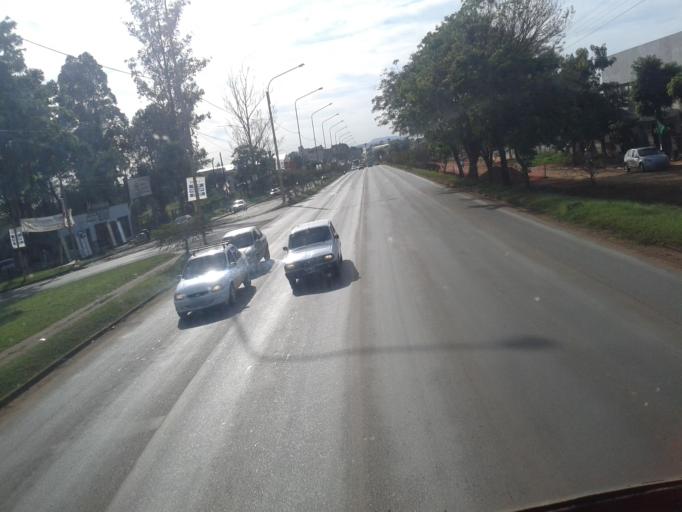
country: AR
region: Misiones
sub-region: Departamento de Capital
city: Posadas
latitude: -27.4037
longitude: -55.9101
